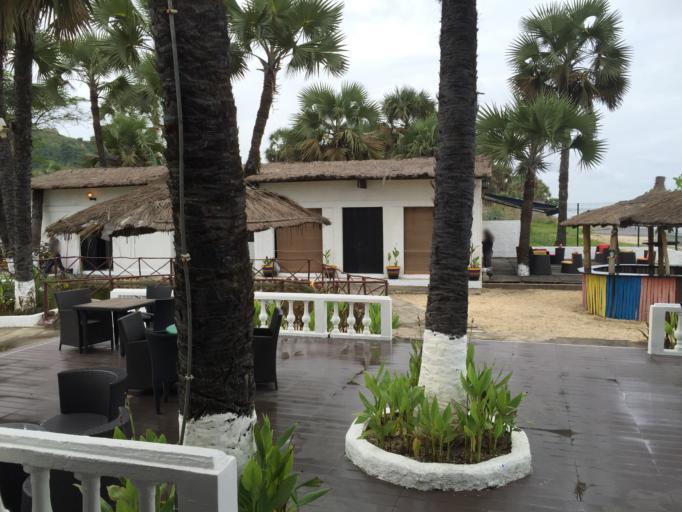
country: AO
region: Cabinda
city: Cabinda
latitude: -5.4399
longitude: 12.2137
